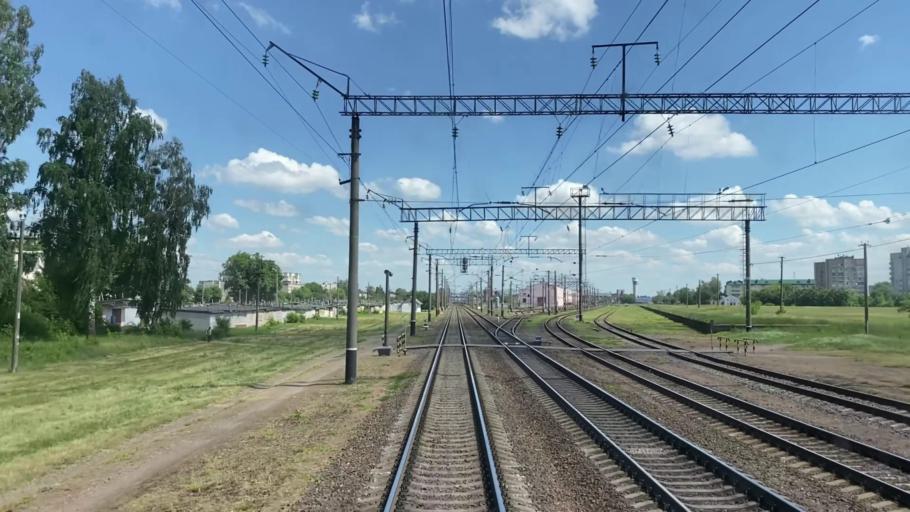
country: BY
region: Brest
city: Baranovichi
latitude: 53.1151
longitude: 25.9655
